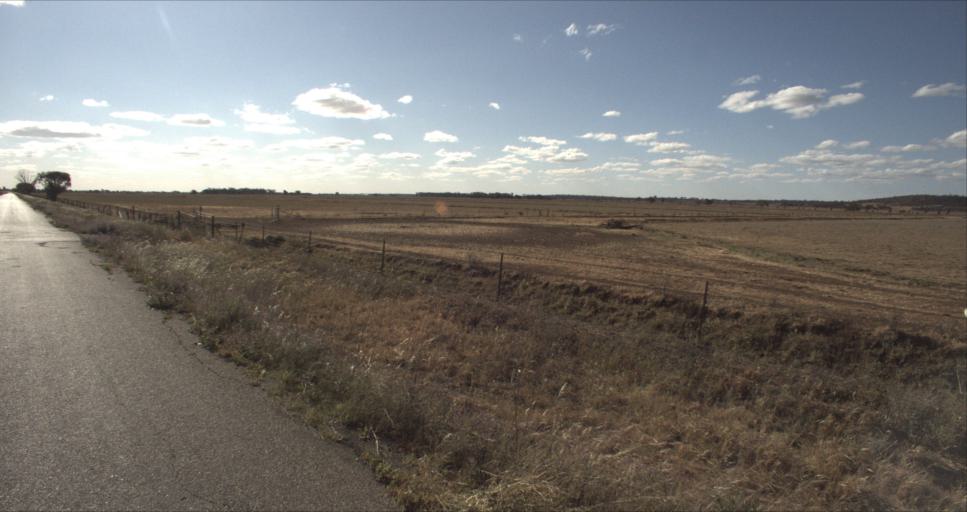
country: AU
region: New South Wales
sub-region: Leeton
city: Leeton
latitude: -34.4429
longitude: 146.2456
